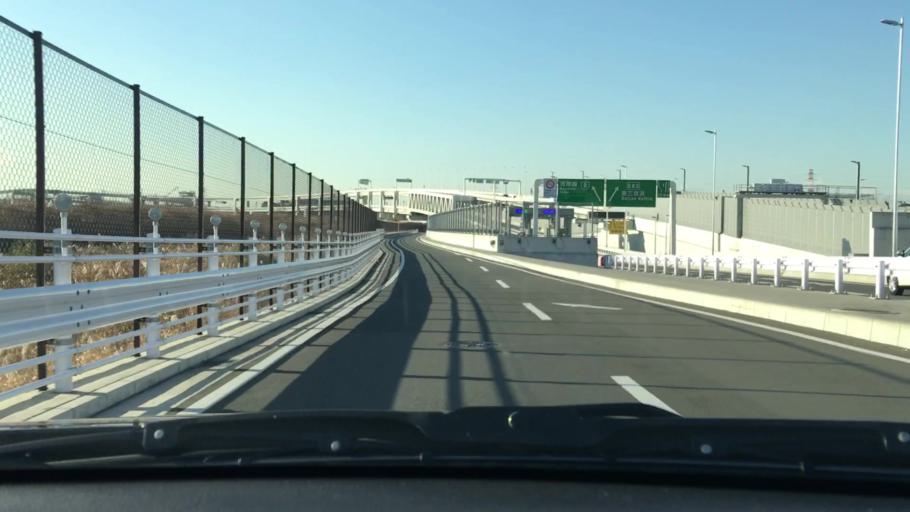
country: JP
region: Kanagawa
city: Yokohama
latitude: 35.5158
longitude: 139.6070
